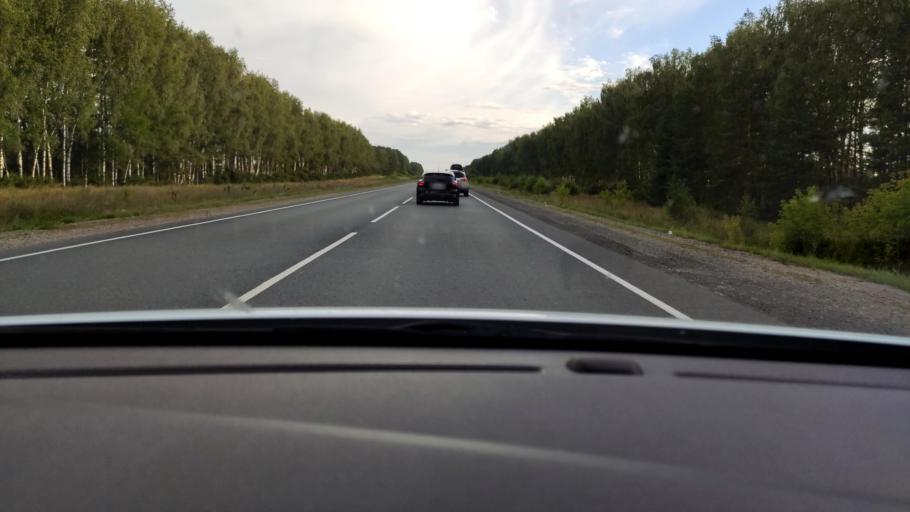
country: RU
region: Mariy-El
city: Pomary
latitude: 55.9806
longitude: 48.3746
